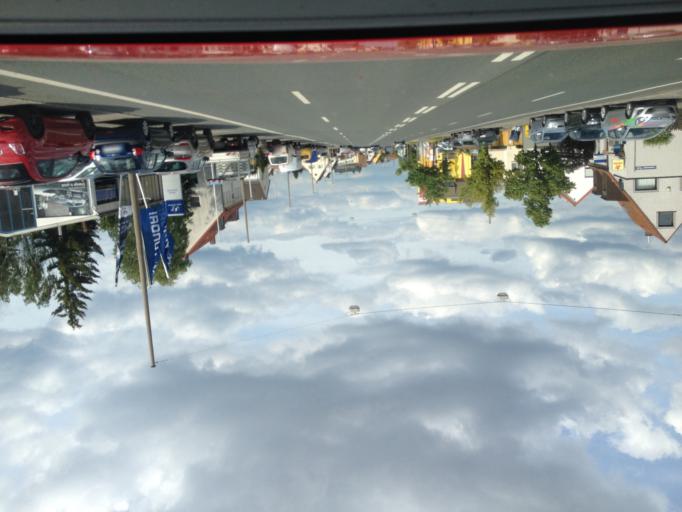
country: DE
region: Bavaria
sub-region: Regierungsbezirk Mittelfranken
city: Grossreuth bei Schweinau
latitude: 49.4522
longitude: 11.0253
